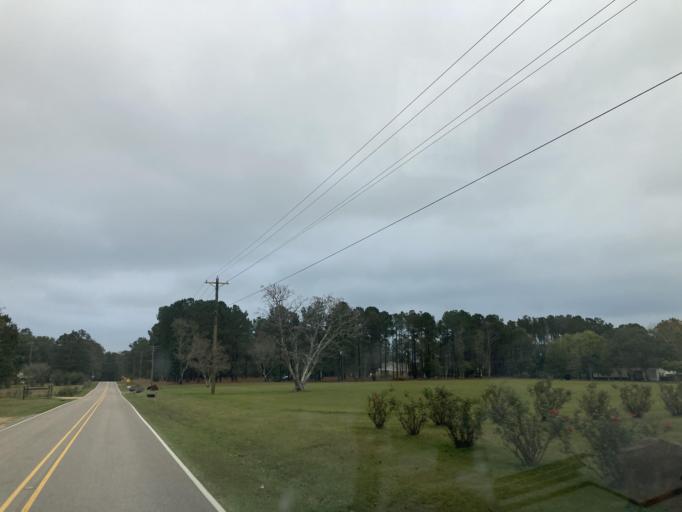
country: US
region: Mississippi
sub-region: Lamar County
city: Purvis
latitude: 31.1636
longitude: -89.4317
